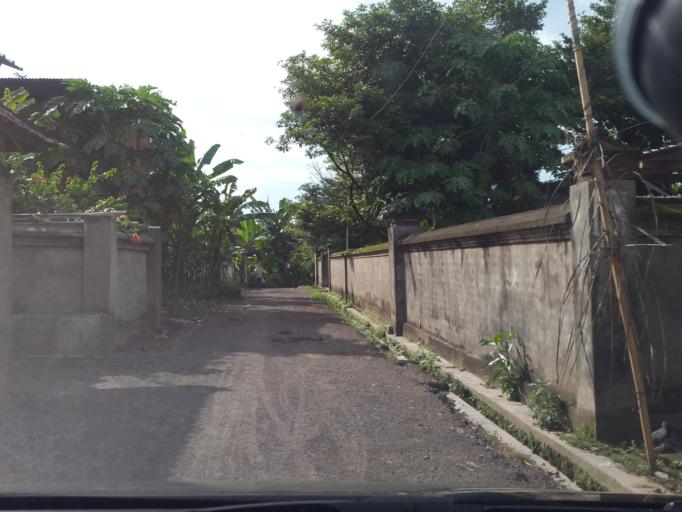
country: ID
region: West Nusa Tenggara
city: Ranggagata
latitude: -8.7023
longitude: 116.1367
